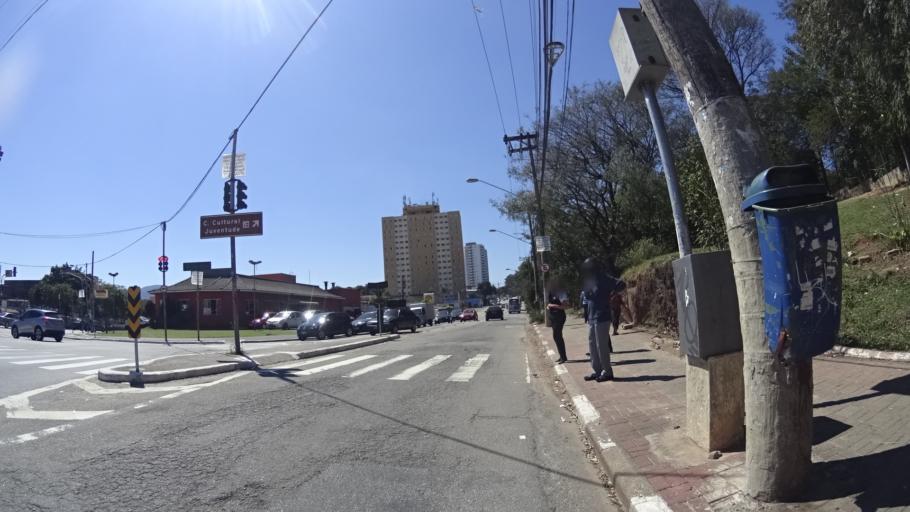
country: BR
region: Sao Paulo
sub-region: Sao Paulo
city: Sao Paulo
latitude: -23.4802
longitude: -46.6730
